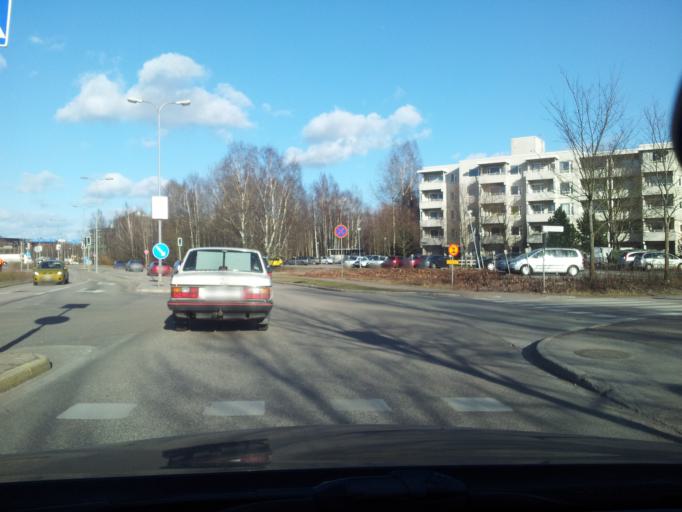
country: FI
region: Uusimaa
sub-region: Helsinki
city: Otaniemi
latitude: 60.1847
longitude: 24.8058
